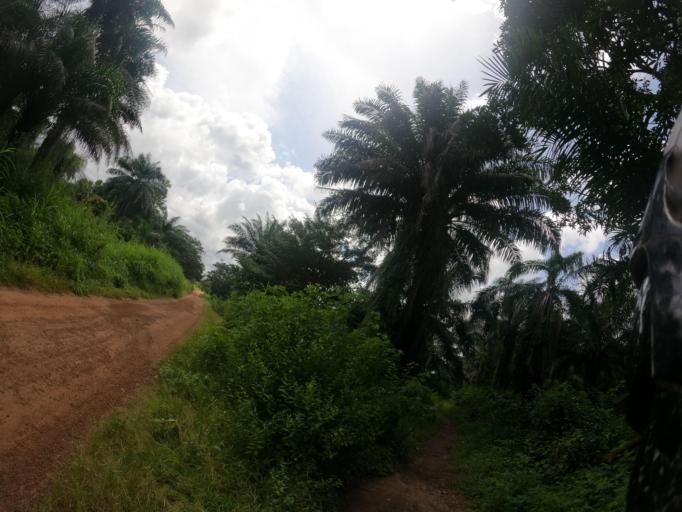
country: SL
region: Northern Province
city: Makeni
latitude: 9.1294
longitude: -12.2700
